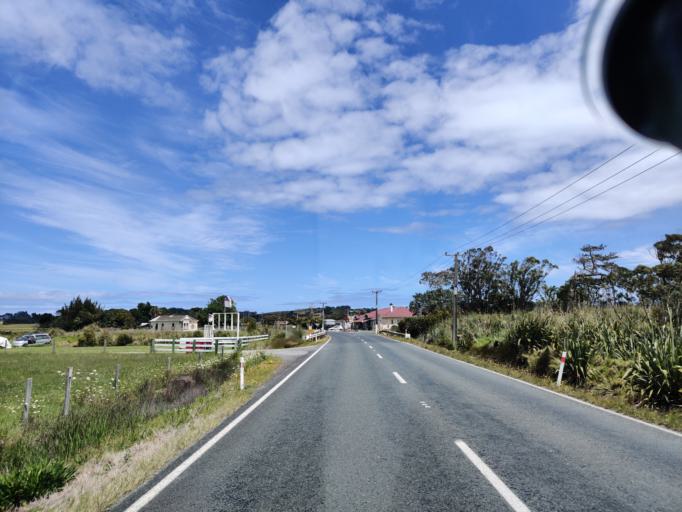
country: NZ
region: Northland
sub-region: Far North District
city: Kaitaia
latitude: -35.0248
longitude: 173.2309
